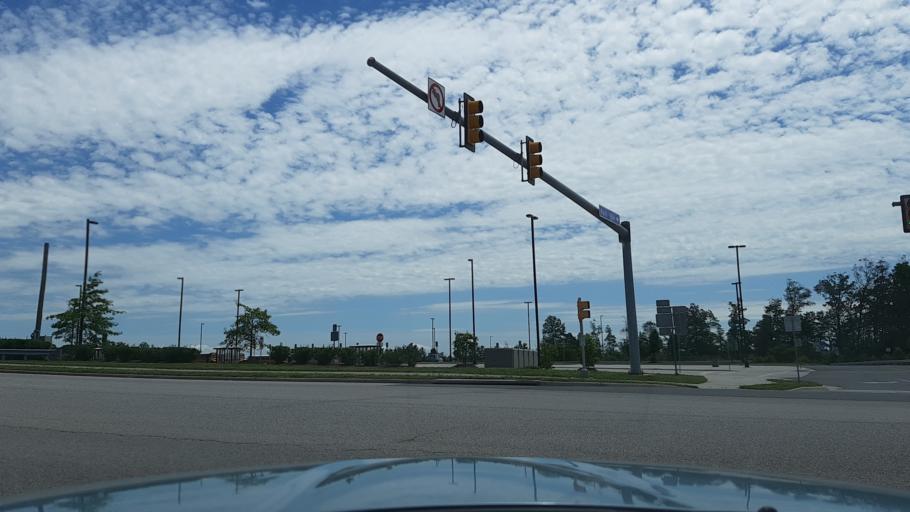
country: US
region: Virginia
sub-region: Fairfax County
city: Newington
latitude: 38.7460
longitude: -77.2107
